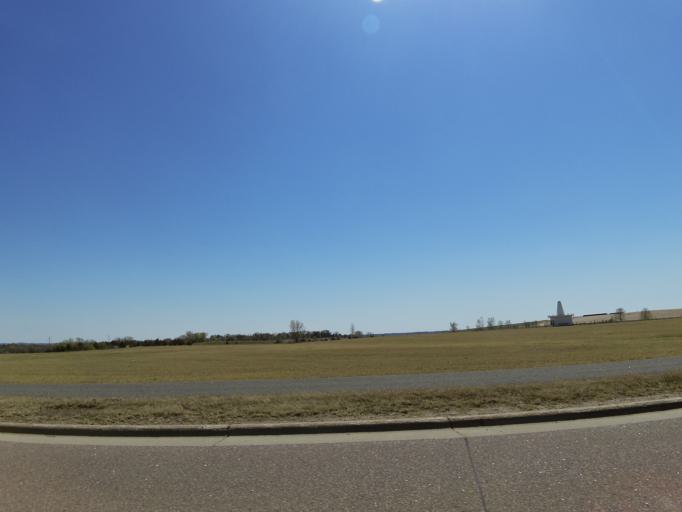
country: US
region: Minnesota
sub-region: Hennepin County
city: Eden Prairie
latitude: 44.8270
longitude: -93.4423
